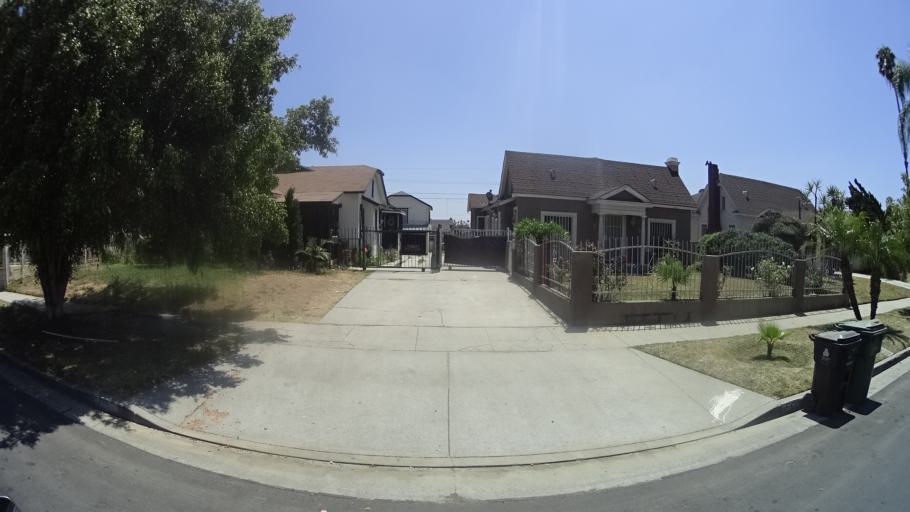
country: US
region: California
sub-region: Los Angeles County
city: View Park-Windsor Hills
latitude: 33.9905
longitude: -118.3247
